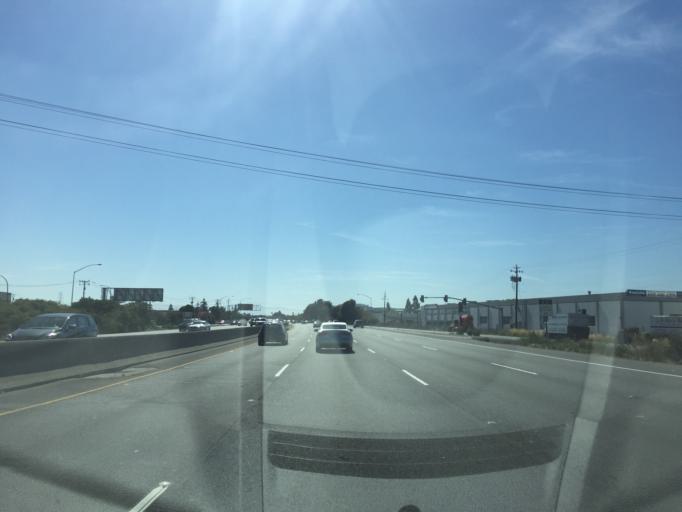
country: US
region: California
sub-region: San Mateo County
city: North Fair Oaks
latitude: 37.4884
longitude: -122.2110
